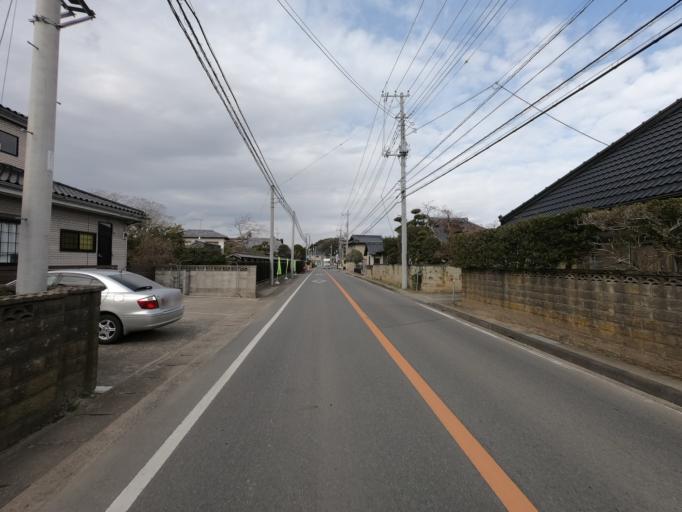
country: JP
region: Ibaraki
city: Inashiki
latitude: 36.0887
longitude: 140.4248
